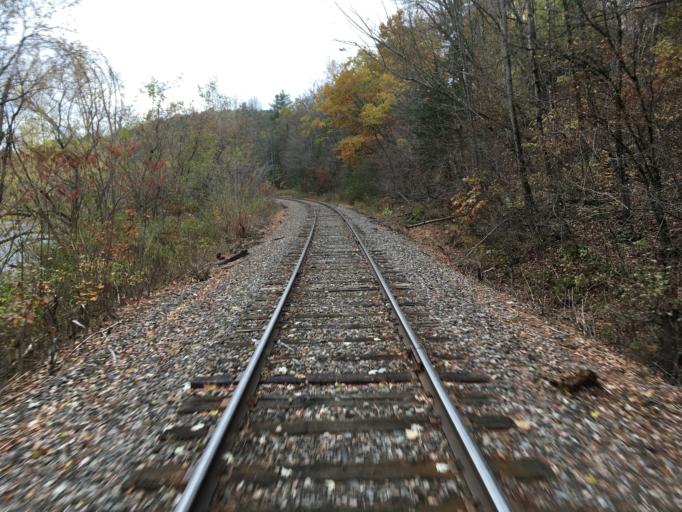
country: US
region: New Hampshire
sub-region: Grafton County
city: Woodsville
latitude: 44.1911
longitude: -72.0664
